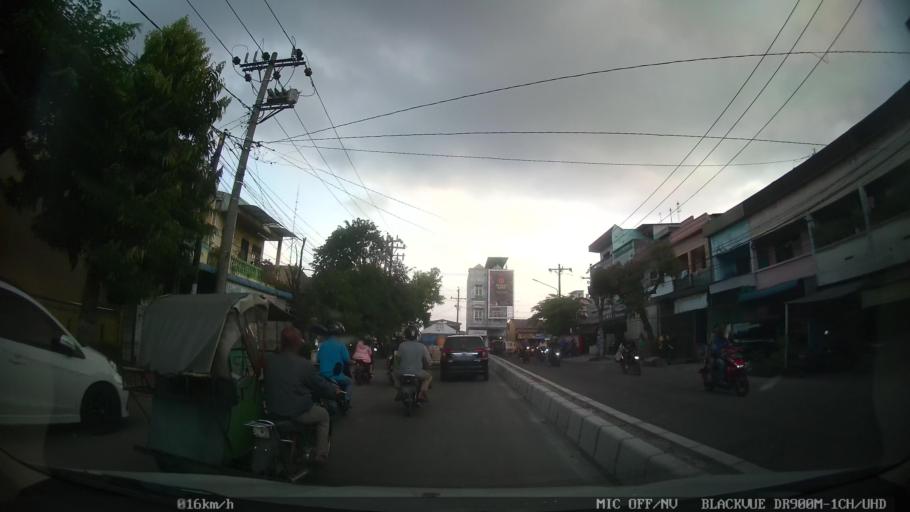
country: ID
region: North Sumatra
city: Medan
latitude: 3.5826
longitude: 98.7112
